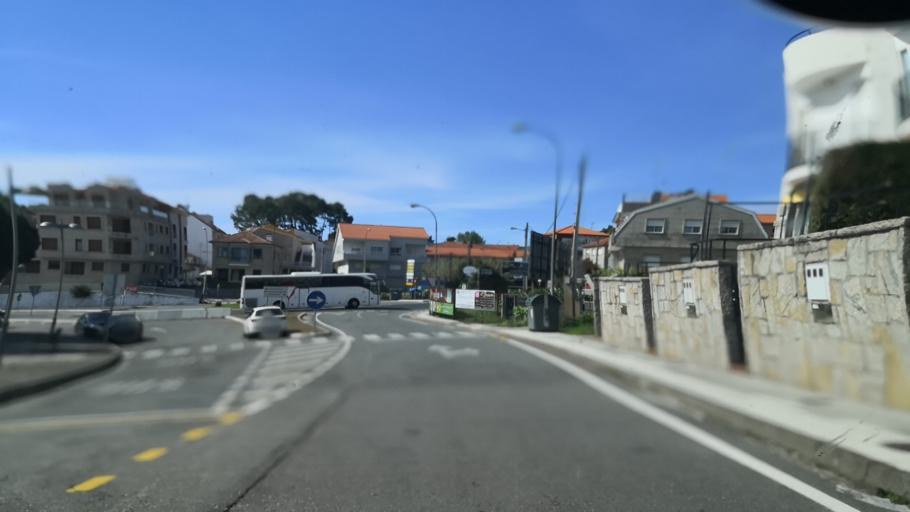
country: ES
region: Galicia
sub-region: Provincia de Pontevedra
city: Sanxenxo
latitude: 42.4000
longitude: -8.8189
